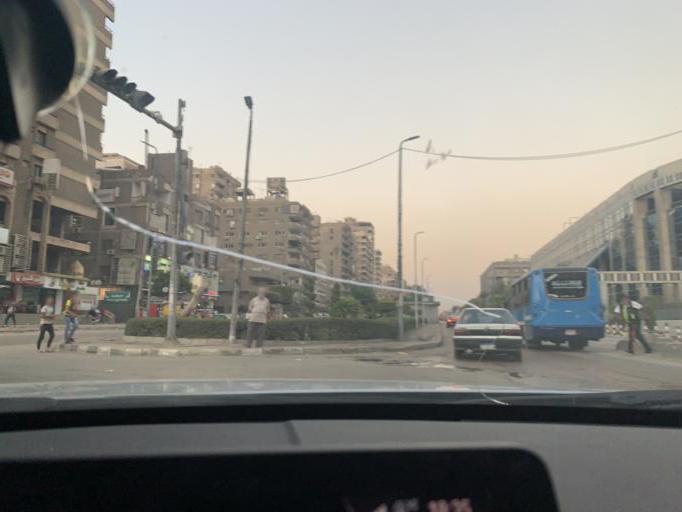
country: EG
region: Muhafazat al Qahirah
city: Cairo
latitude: 30.0447
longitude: 31.3398
